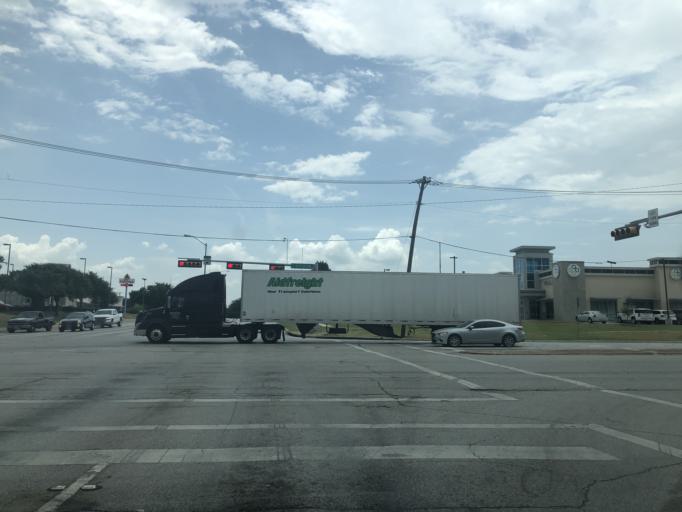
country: US
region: Texas
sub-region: Dallas County
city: Grand Prairie
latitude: 32.7419
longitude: -97.0157
